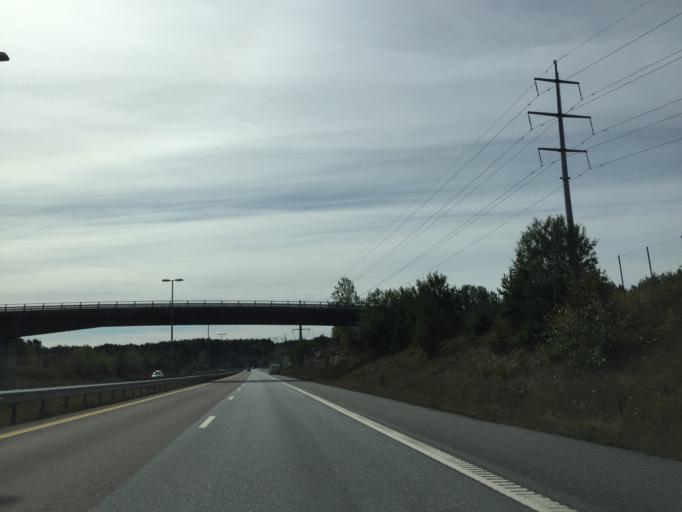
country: NO
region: Akershus
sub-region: Vestby
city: Vestby
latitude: 59.5433
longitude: 10.7247
